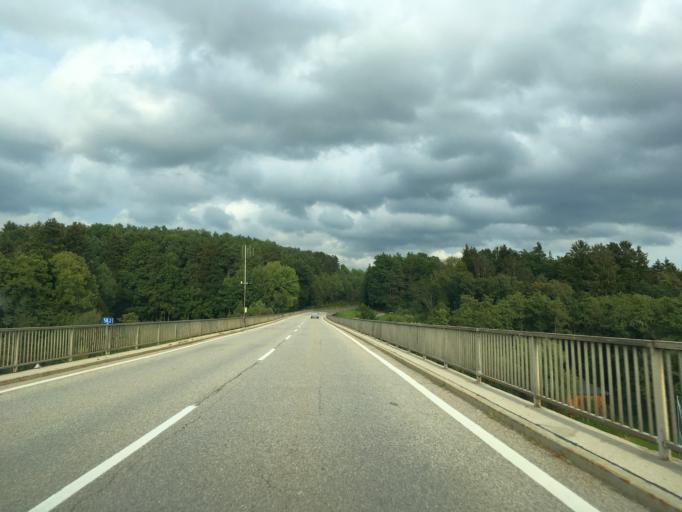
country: AT
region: Styria
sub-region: Politischer Bezirk Hartberg-Fuerstenfeld
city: Dechantskirchen
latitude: 47.4155
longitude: 16.0259
